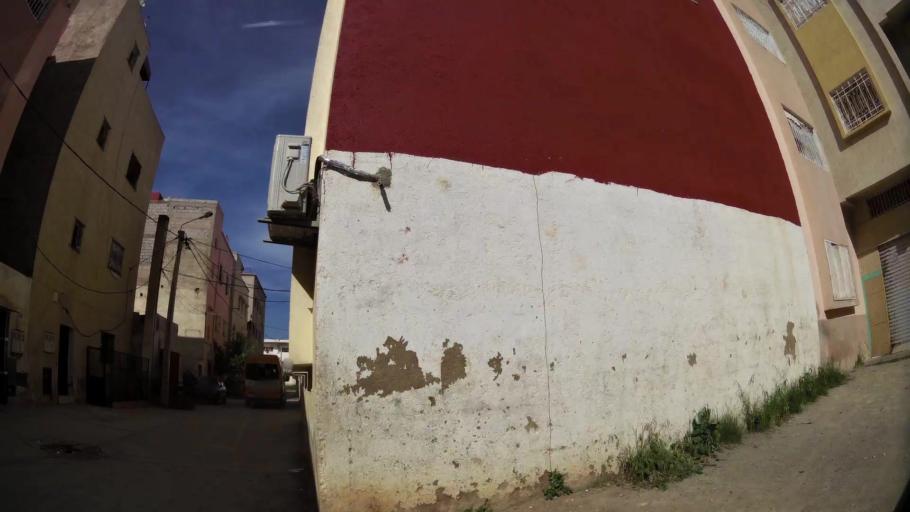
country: MA
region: Fes-Boulemane
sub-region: Fes
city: Fes
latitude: 34.0244
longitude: -5.0332
